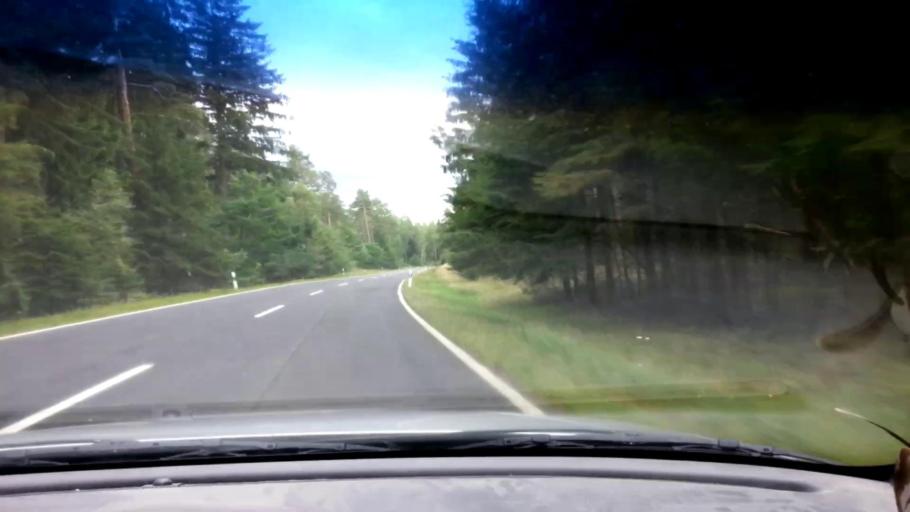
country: DE
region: Bavaria
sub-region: Upper Palatinate
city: Waldsassen
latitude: 50.0211
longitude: 12.3111
